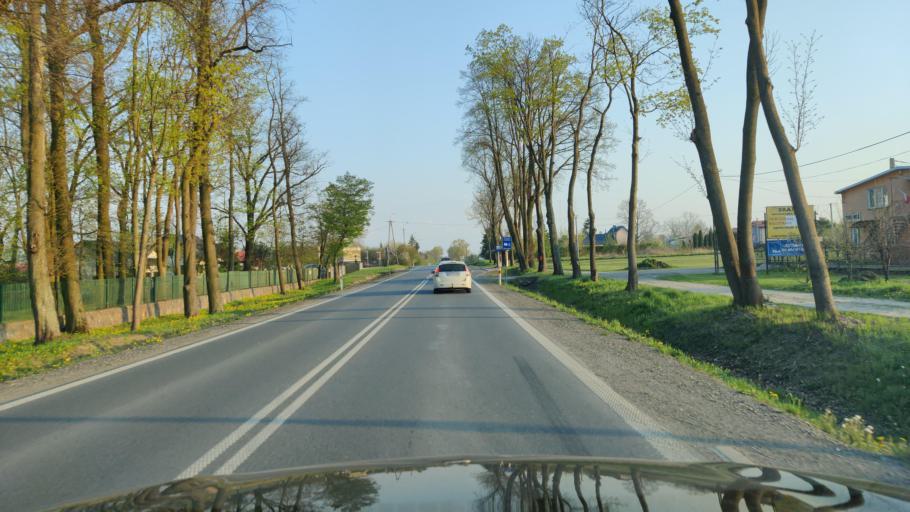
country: PL
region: Masovian Voivodeship
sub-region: Powiat pultuski
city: Pultusk
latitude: 52.6712
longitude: 21.0813
